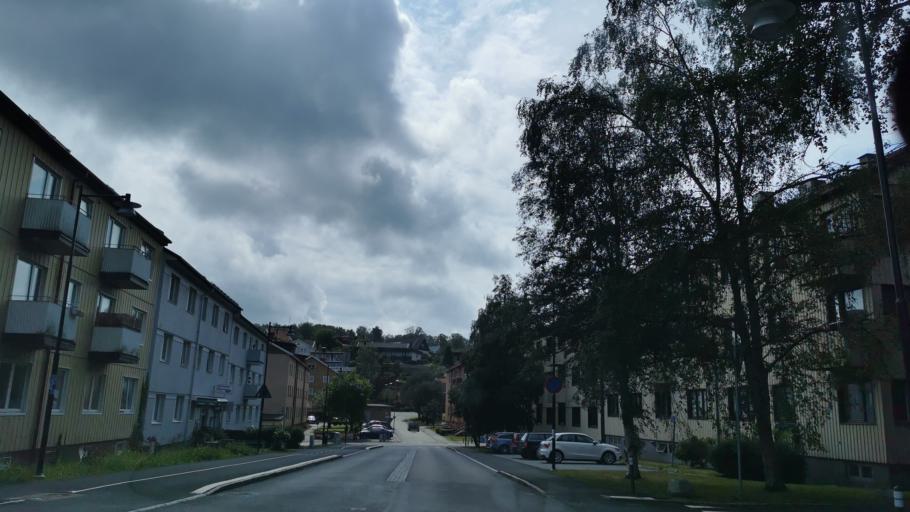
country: SE
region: Vaestra Goetaland
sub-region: Molndal
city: Moelndal
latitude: 57.6767
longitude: 11.9931
